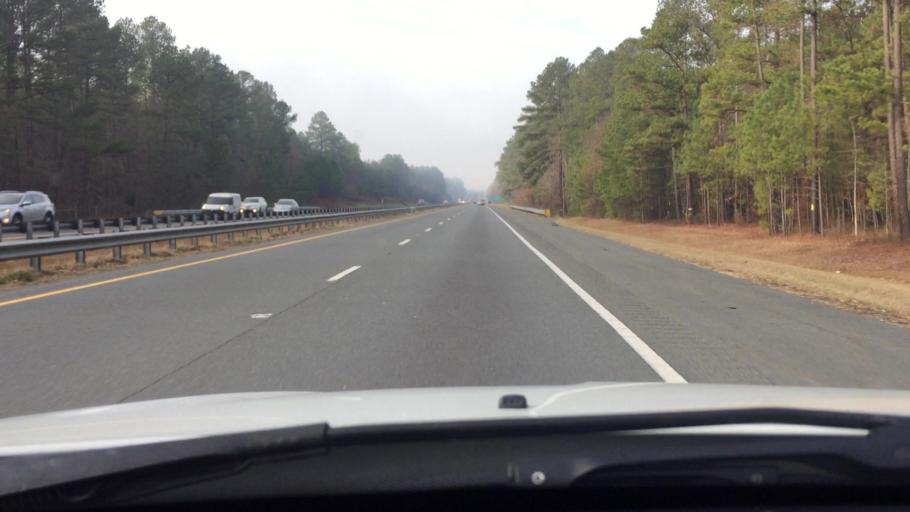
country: US
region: North Carolina
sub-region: Chatham County
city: Pittsboro
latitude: 35.6419
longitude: -79.0273
